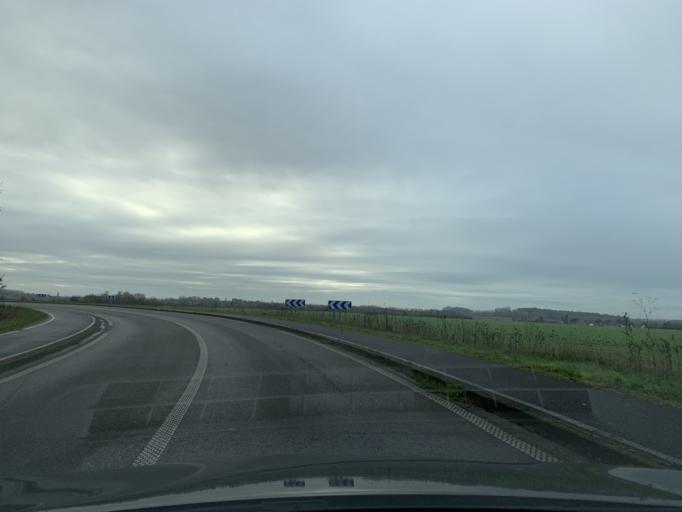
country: FR
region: Nord-Pas-de-Calais
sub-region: Departement du Nord
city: Goeulzin
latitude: 50.3251
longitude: 3.1090
